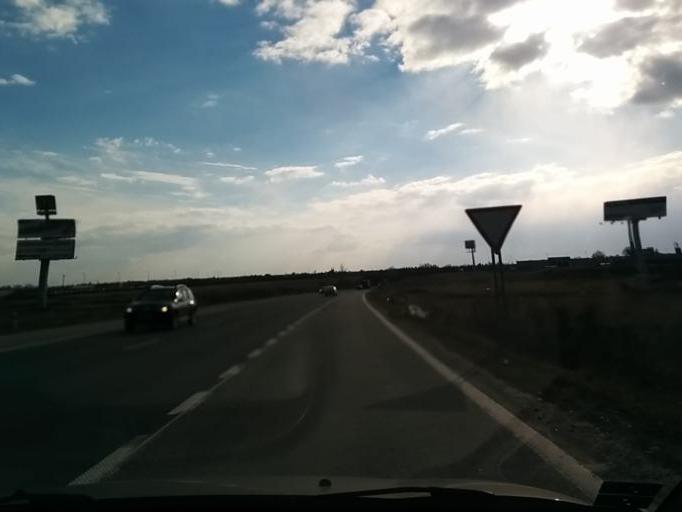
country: SK
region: Trnavsky
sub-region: Okres Trnava
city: Trnava
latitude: 48.3670
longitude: 17.6190
